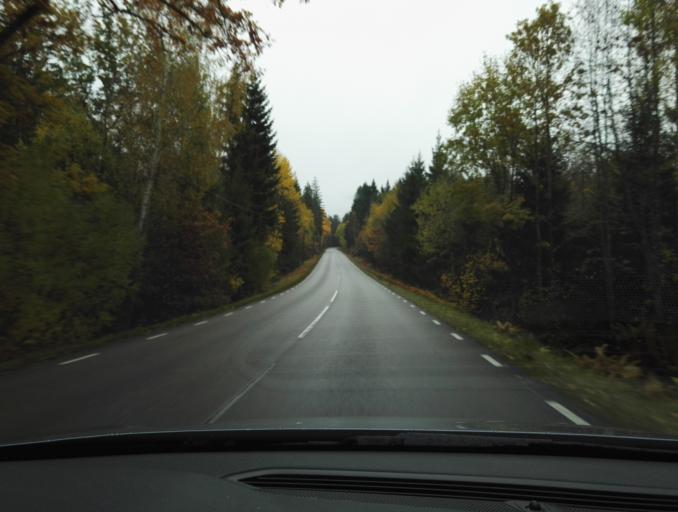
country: SE
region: Kronoberg
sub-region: Vaxjo Kommun
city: Rottne
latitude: 57.0289
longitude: 14.8200
